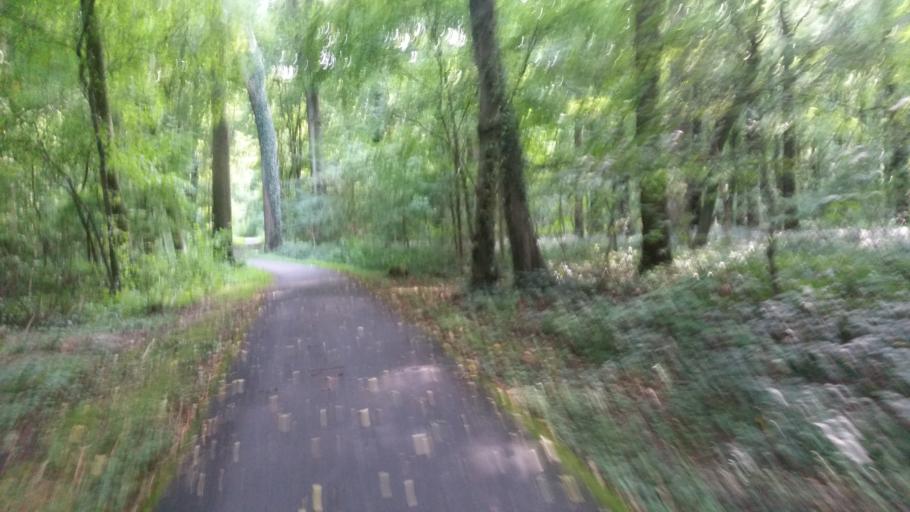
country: DE
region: Lower Saxony
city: Hannover
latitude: 52.3945
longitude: 9.7713
